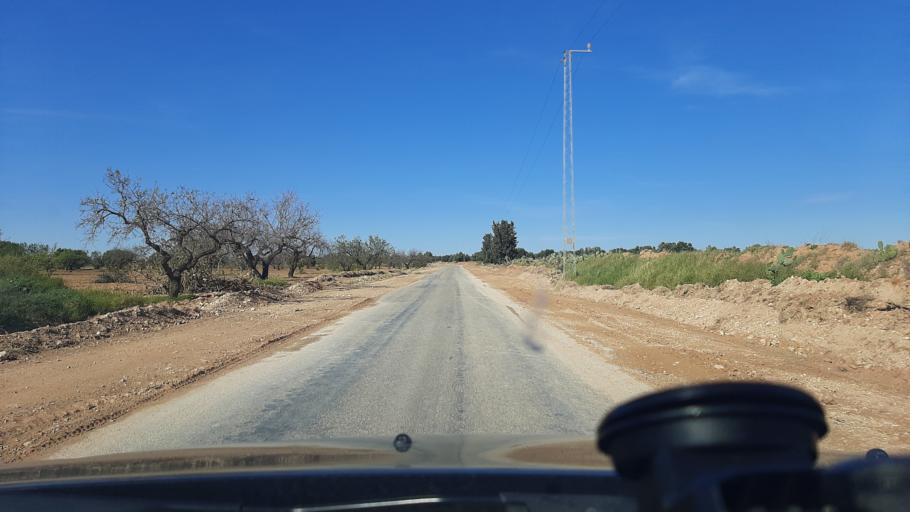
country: TN
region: Safaqis
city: Sfax
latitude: 34.9280
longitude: 10.5729
